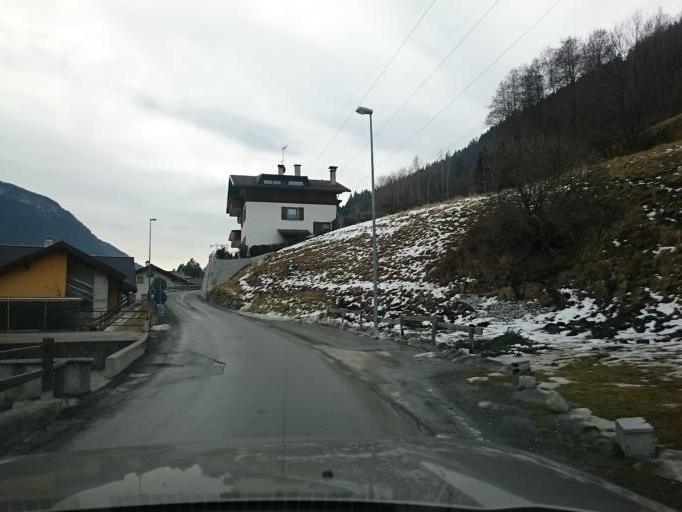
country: IT
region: Lombardy
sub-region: Provincia di Sondrio
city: Cepina
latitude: 46.4521
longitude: 10.3567
